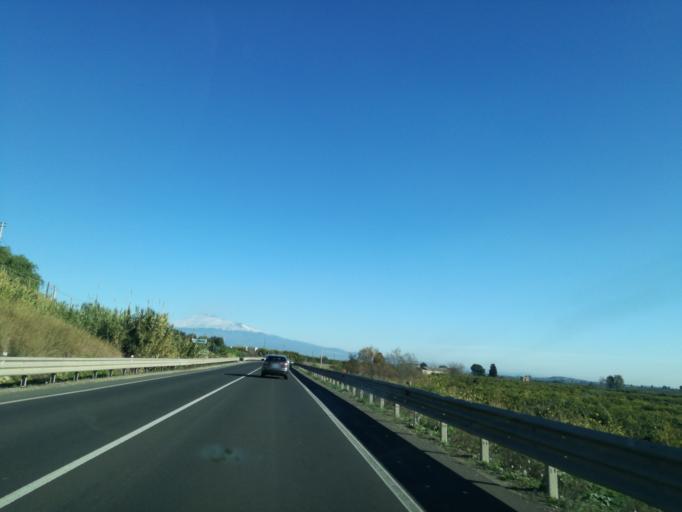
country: IT
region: Sicily
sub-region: Catania
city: Ramacca
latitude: 37.3740
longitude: 14.7273
